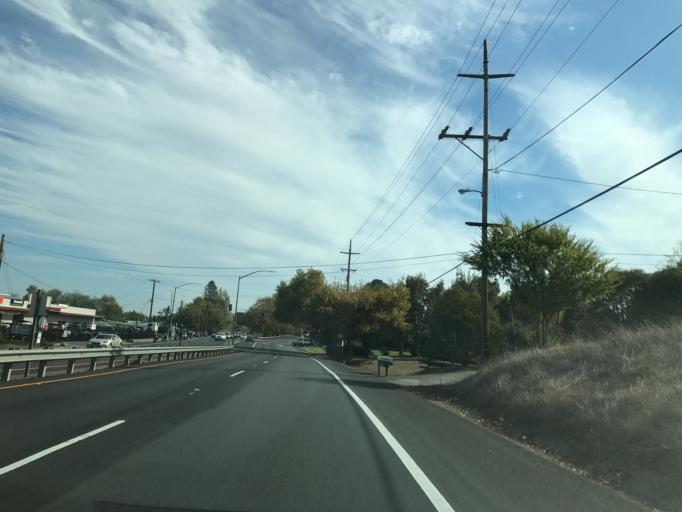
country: US
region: California
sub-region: Sonoma County
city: Petaluma
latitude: 38.2606
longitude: -122.6625
